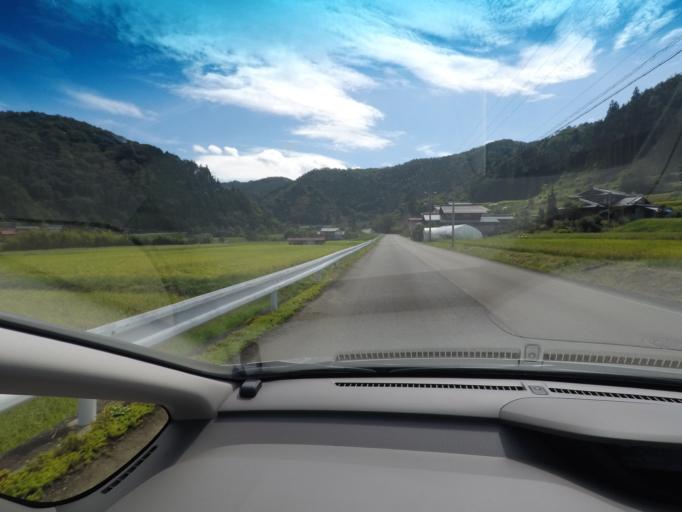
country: JP
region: Gifu
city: Takayama
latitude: 36.1354
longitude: 137.3121
